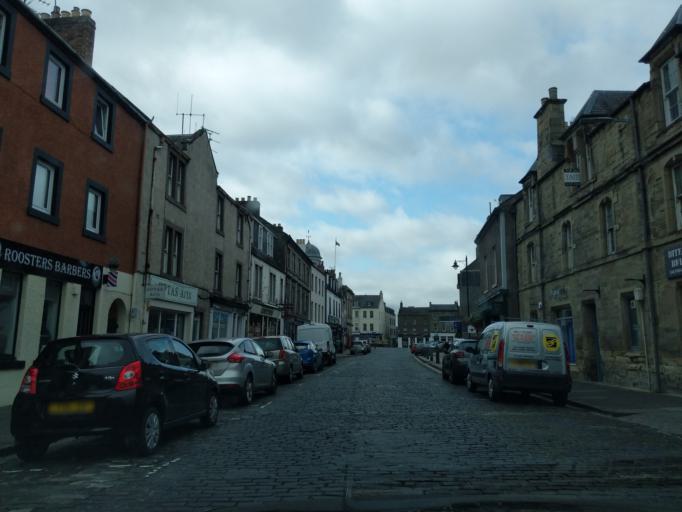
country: GB
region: Scotland
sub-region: The Scottish Borders
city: Kelso
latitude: 55.5992
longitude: -2.4323
